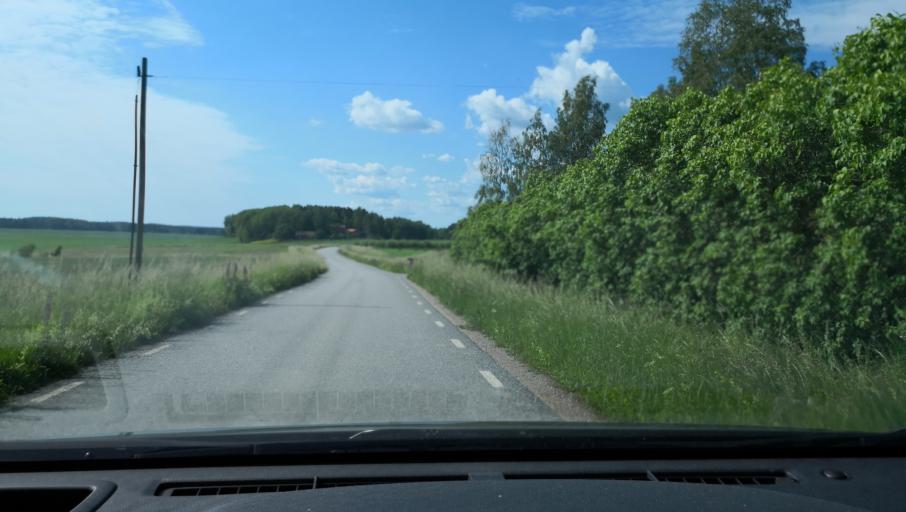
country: SE
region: Uppsala
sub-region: Enkopings Kommun
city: Orsundsbro
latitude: 59.8193
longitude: 17.3304
